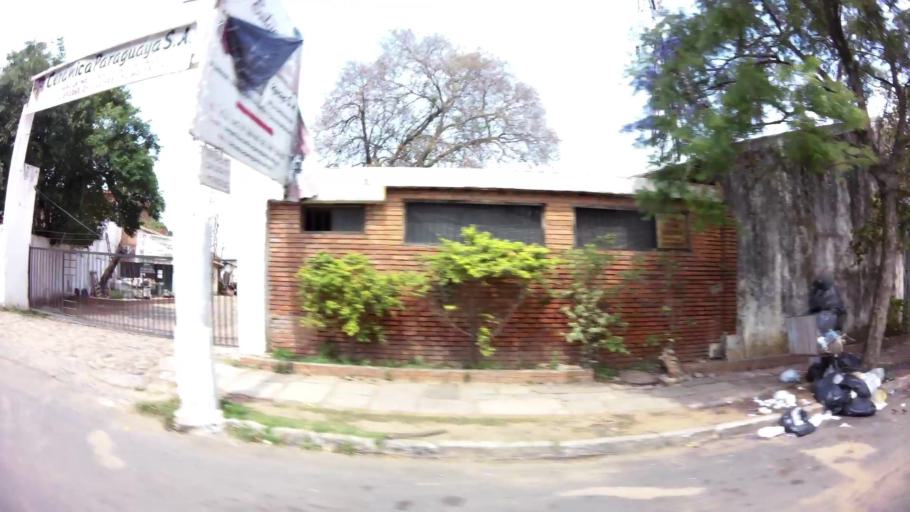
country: PY
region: Asuncion
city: Asuncion
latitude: -25.2604
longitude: -57.5815
